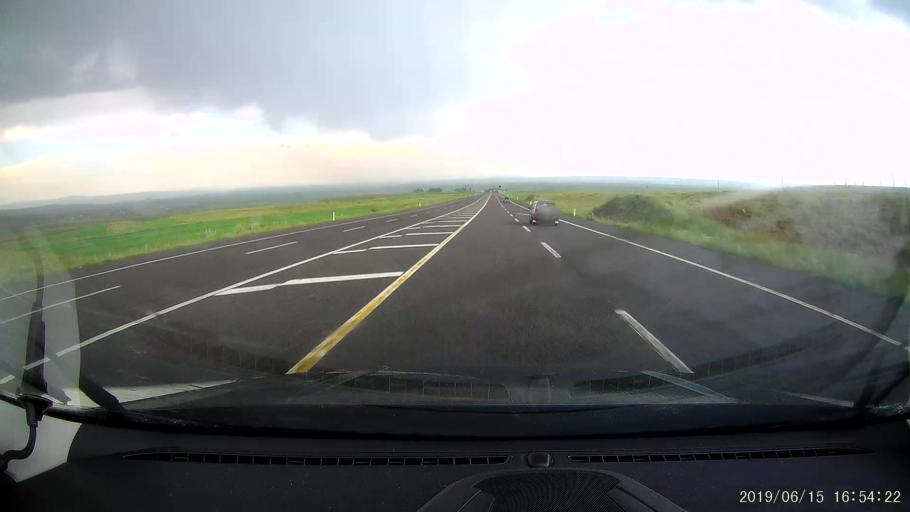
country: TR
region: Kars
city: Susuz
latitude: 40.7908
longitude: 43.1227
